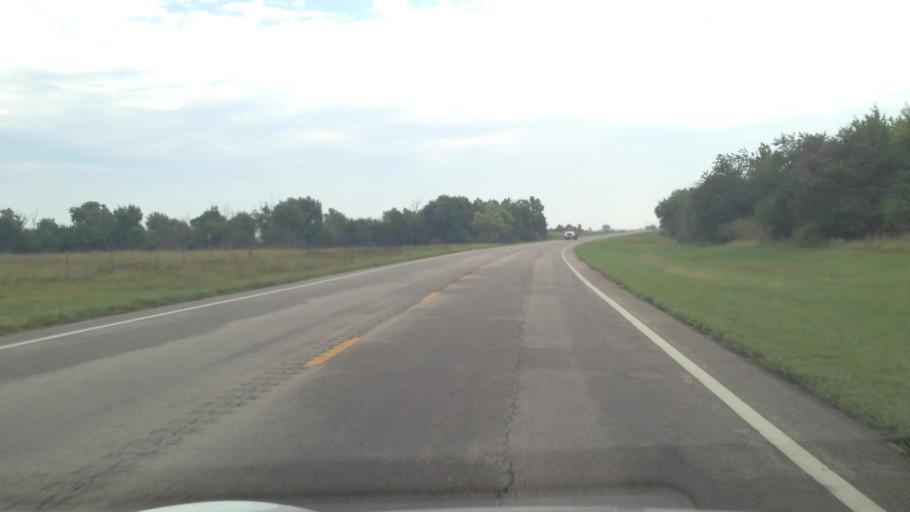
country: US
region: Kansas
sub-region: Bourbon County
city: Fort Scott
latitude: 37.8915
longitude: -95.0388
